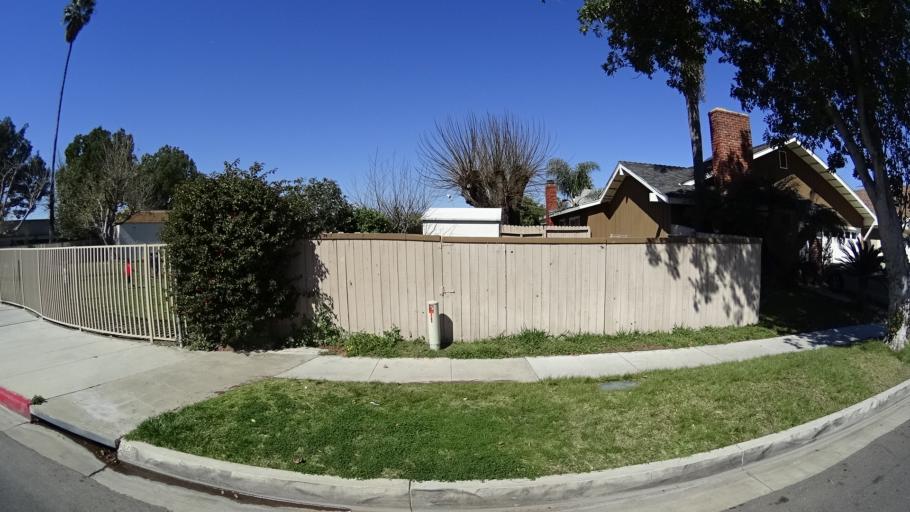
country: US
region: California
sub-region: Orange County
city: Yorba Linda
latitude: 33.8693
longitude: -117.8118
